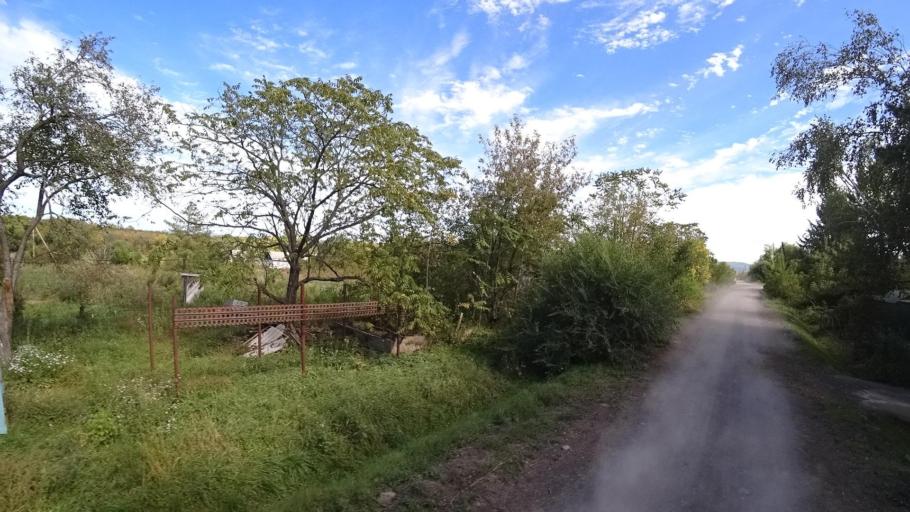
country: RU
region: Primorskiy
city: Yakovlevka
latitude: 44.4357
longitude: 133.5643
